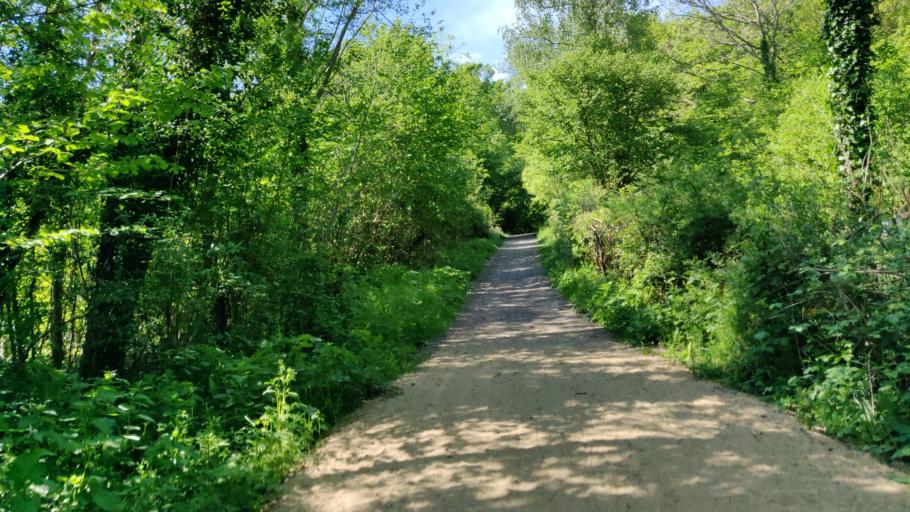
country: GB
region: England
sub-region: West Sussex
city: Rudgwick
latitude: 51.0867
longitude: -0.4464
